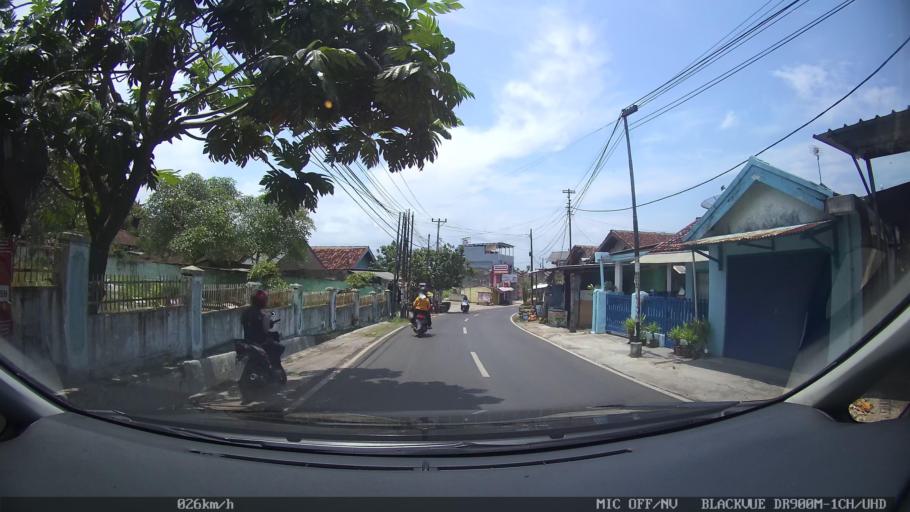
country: ID
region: Lampung
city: Kedaton
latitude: -5.4006
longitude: 105.2557
